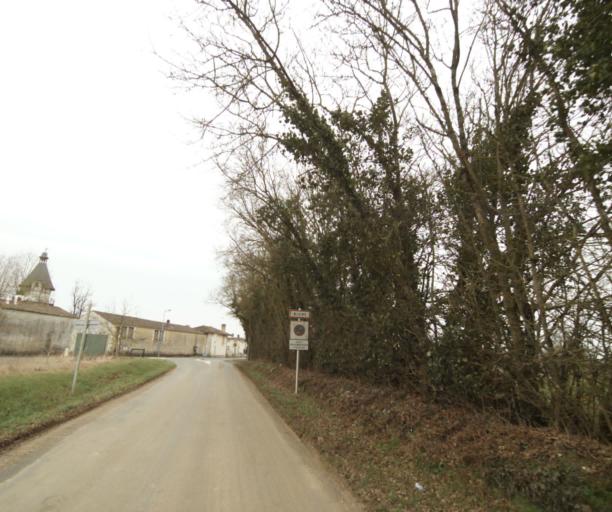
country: FR
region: Poitou-Charentes
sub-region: Departement des Deux-Sevres
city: Magne
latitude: 46.3316
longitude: -0.5205
